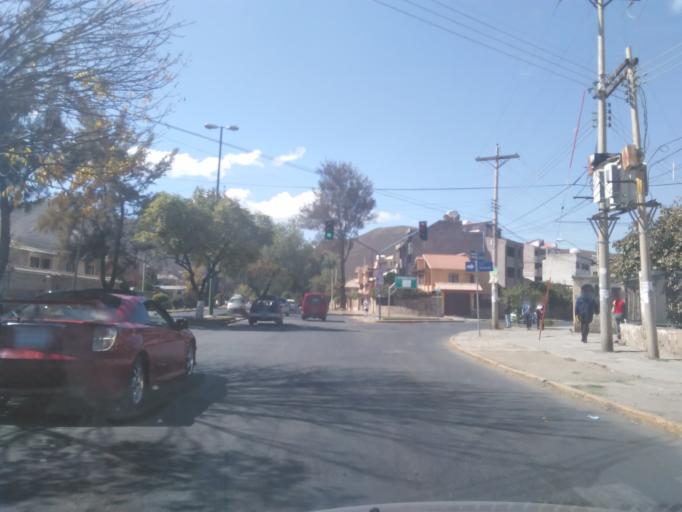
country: BO
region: Cochabamba
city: Cochabamba
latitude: -17.3972
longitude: -66.1455
